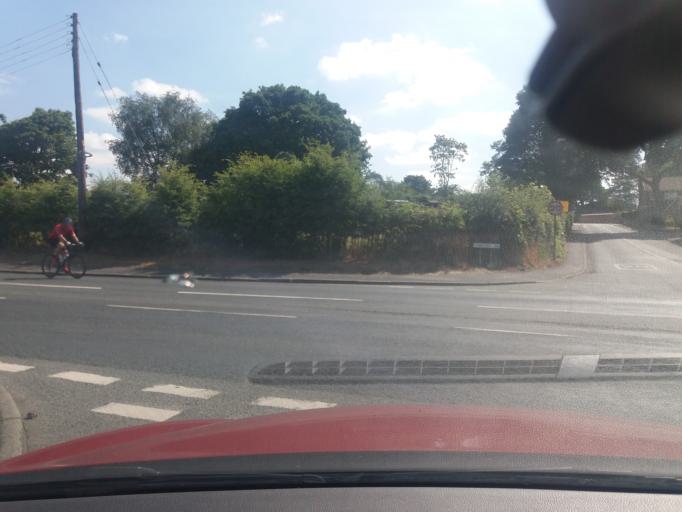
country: GB
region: England
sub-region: Lancashire
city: Adlington
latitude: 53.6225
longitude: -2.6118
